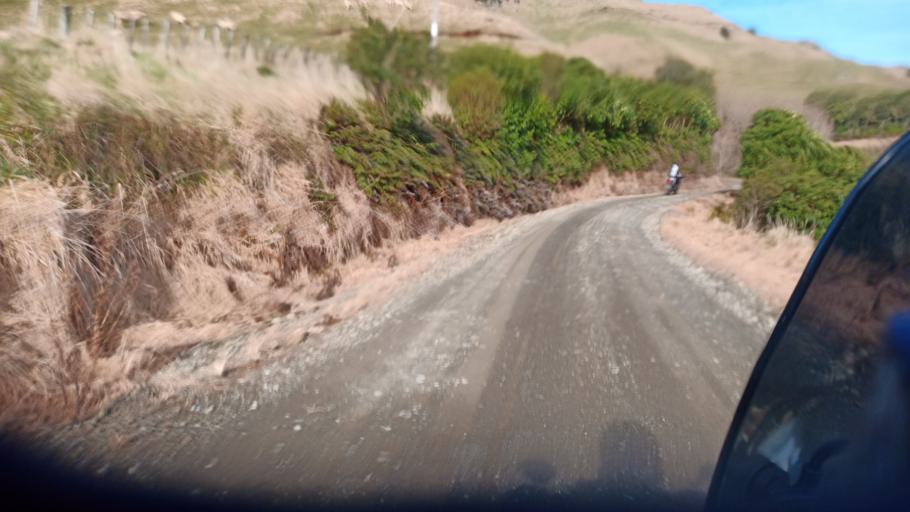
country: NZ
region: Gisborne
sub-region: Gisborne District
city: Gisborne
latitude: -38.4532
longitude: 177.5379
